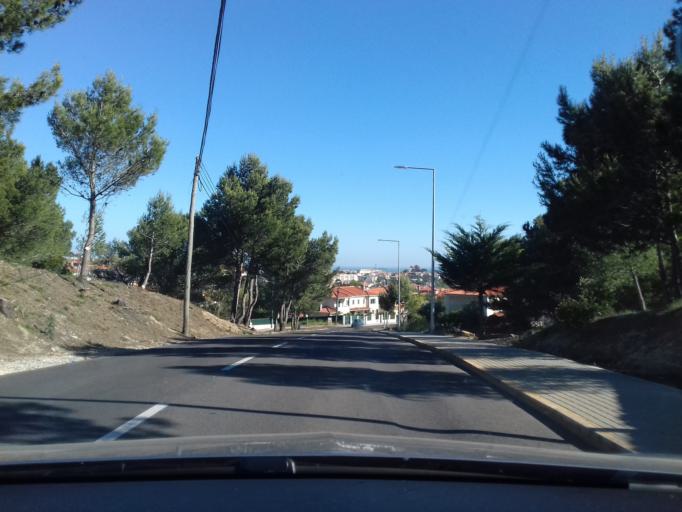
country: PT
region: Lisbon
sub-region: Cascais
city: Alcabideche
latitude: 38.7243
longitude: -9.4134
